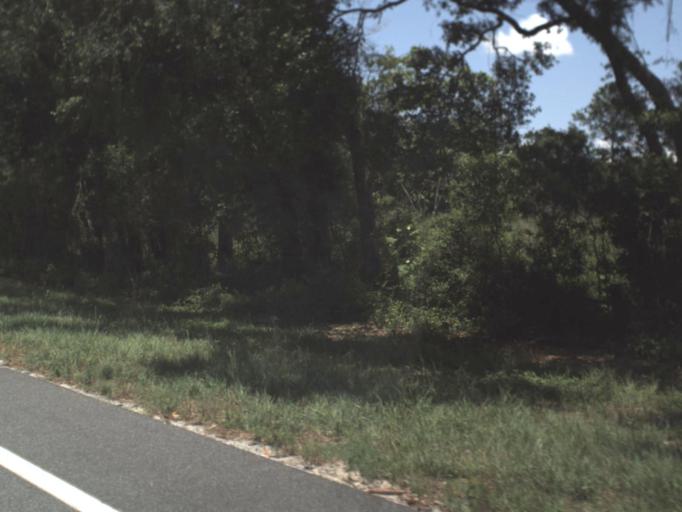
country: US
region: Florida
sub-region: Lafayette County
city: Mayo
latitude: 29.9350
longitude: -82.9491
